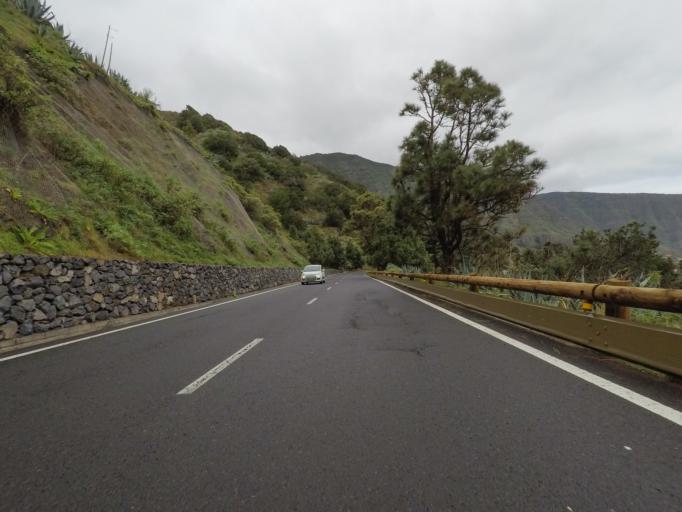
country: ES
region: Canary Islands
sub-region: Provincia de Santa Cruz de Tenerife
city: Hermigua
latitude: 28.1413
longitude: -17.1968
